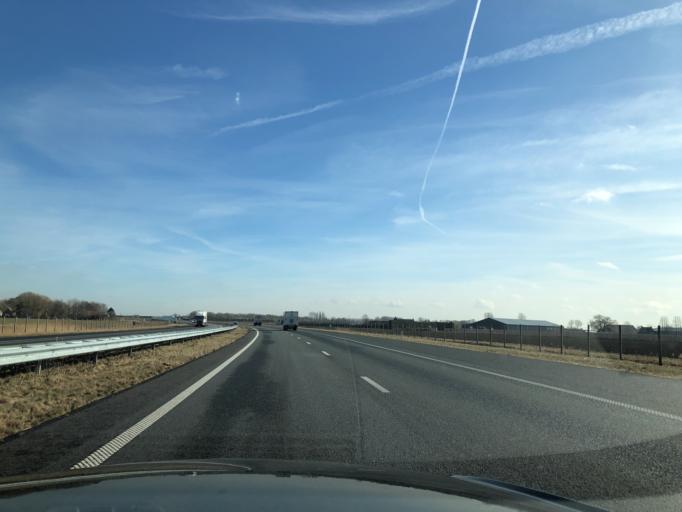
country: NL
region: North Brabant
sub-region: Gemeente Steenbergen
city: Welberg
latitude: 51.5970
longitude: 4.3508
